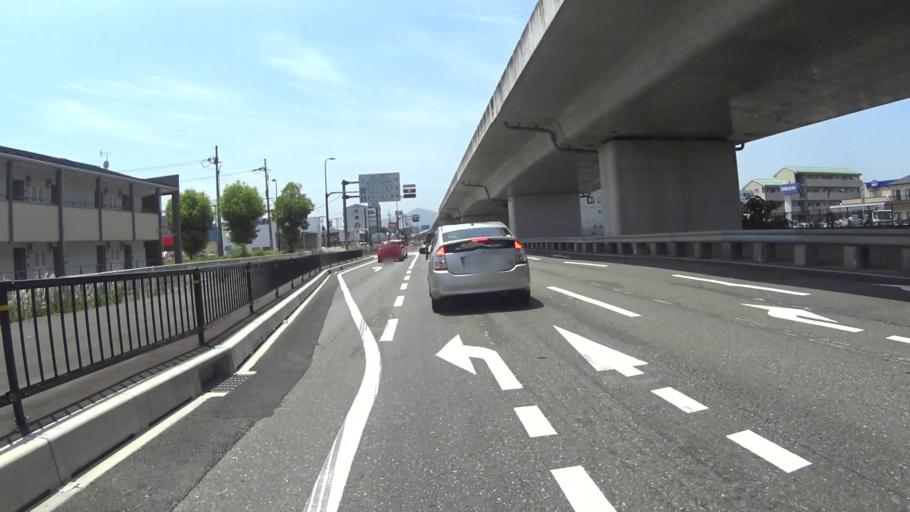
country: JP
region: Kyoto
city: Fukuchiyama
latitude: 35.2903
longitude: 135.1389
